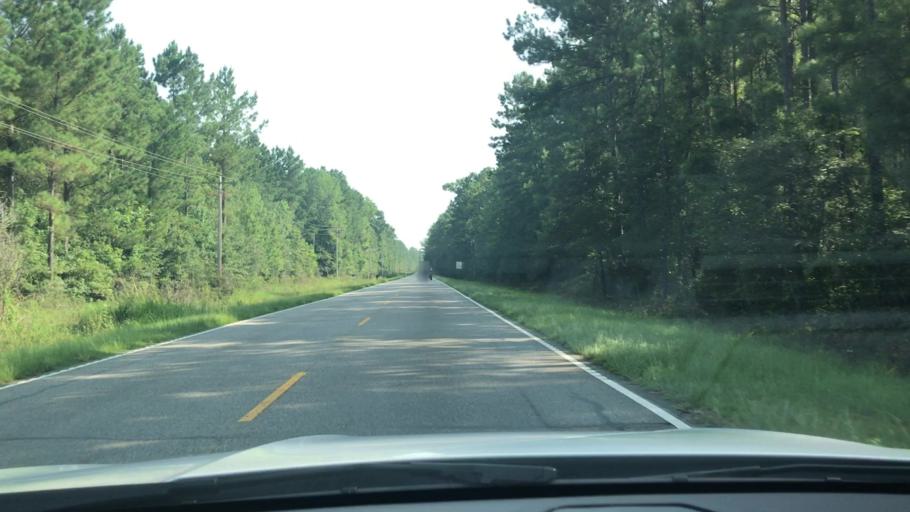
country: US
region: South Carolina
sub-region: Georgetown County
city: Georgetown
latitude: 33.4881
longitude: -79.2661
